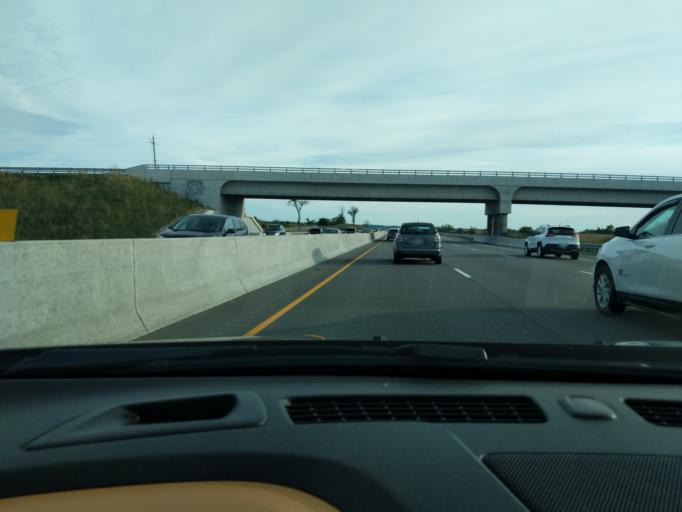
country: CA
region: Ontario
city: Innisfil
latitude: 44.2376
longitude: -79.6670
